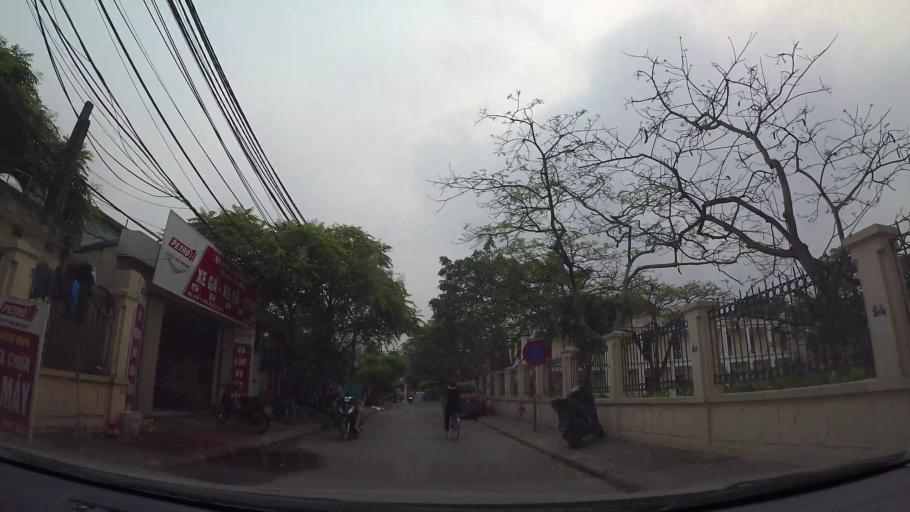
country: VN
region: Ha Noi
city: Hoan Kiem
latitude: 21.0650
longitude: 105.8934
